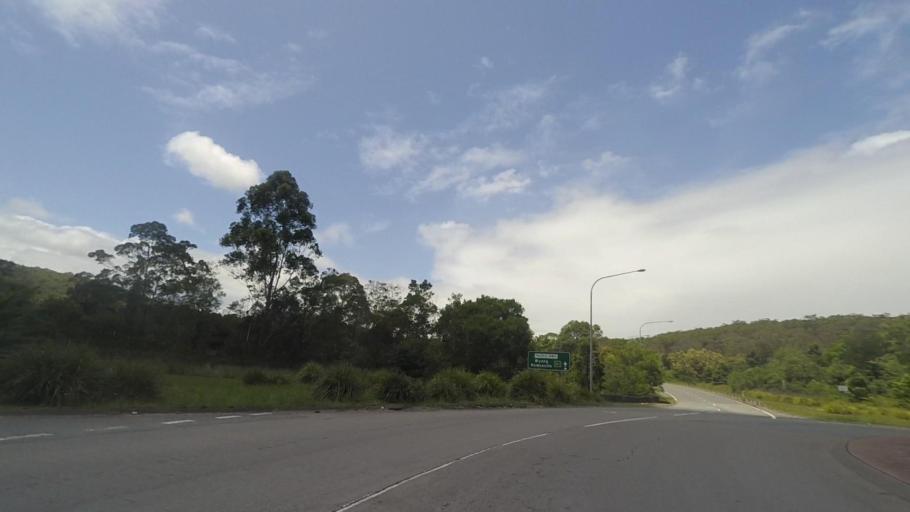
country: AU
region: New South Wales
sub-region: Gosford Shire
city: Lisarow
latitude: -33.3441
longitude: 151.3683
